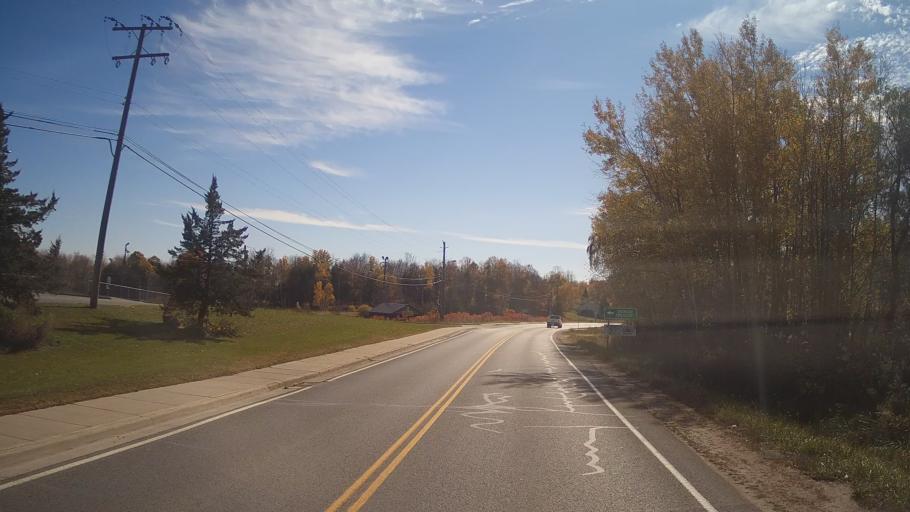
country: CA
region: Ontario
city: Perth
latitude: 44.7807
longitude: -76.6828
